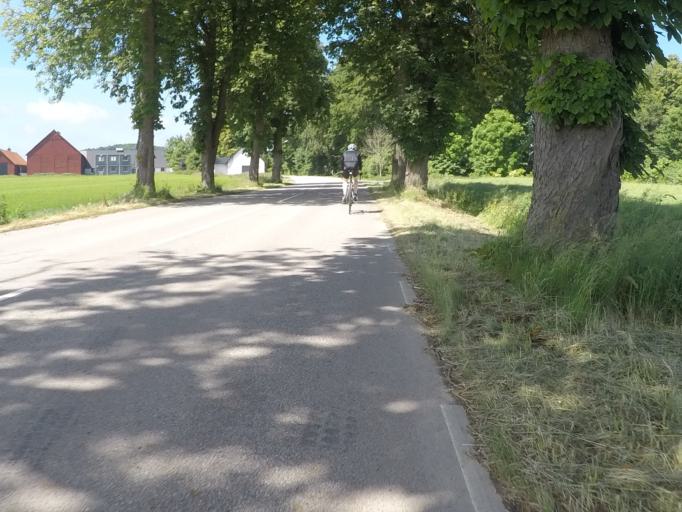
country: SE
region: Skane
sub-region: Malmo
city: Oxie
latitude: 55.5284
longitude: 13.1512
